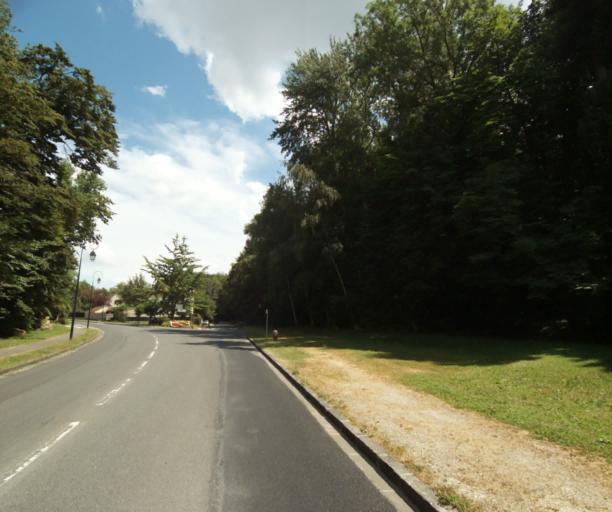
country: FR
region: Ile-de-France
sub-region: Departement de Seine-et-Marne
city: Samoreau
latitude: 48.4292
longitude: 2.7596
